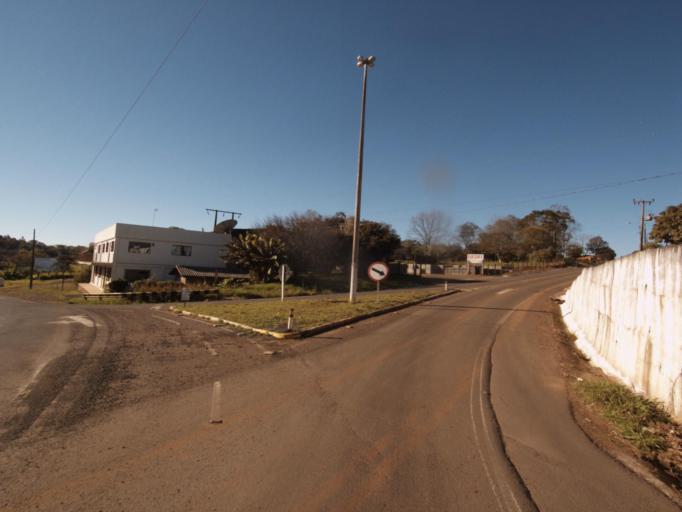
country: AR
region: Misiones
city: Bernardo de Irigoyen
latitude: -26.6562
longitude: -53.5170
